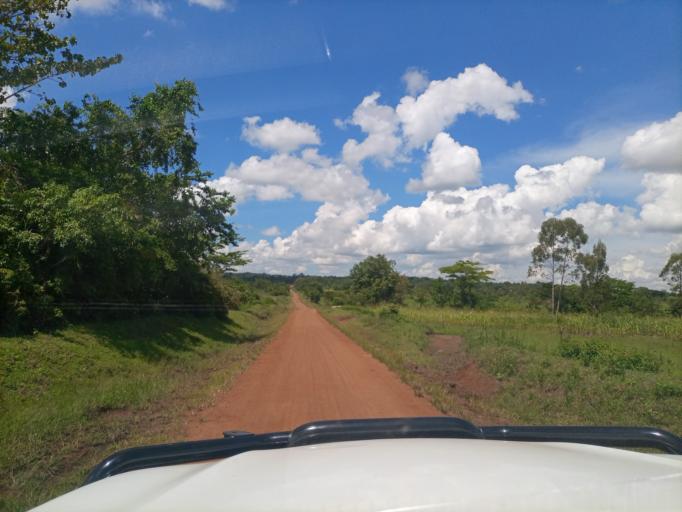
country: UG
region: Eastern Region
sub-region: Tororo District
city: Tororo
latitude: 0.7175
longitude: 34.0154
